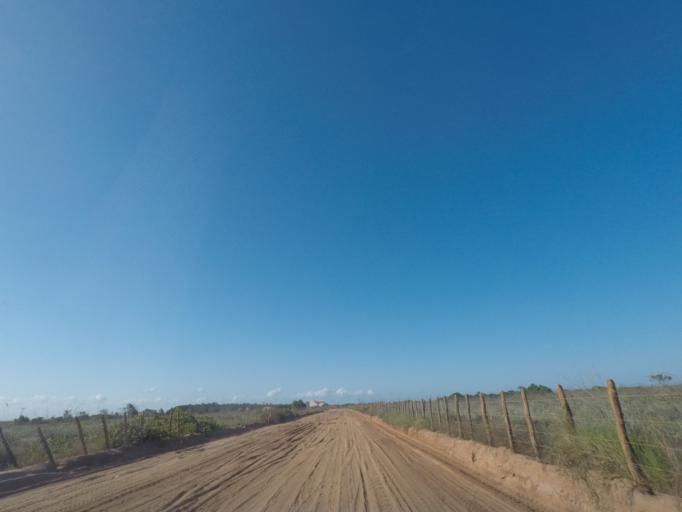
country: BR
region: Bahia
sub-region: Camamu
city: Camamu
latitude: -13.9400
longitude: -38.9459
